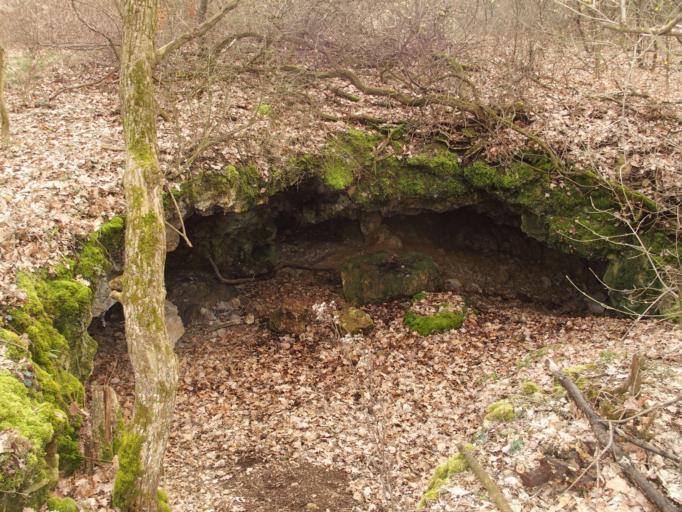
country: HU
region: Fejer
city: Szabadbattyan
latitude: 47.1008
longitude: 18.3295
